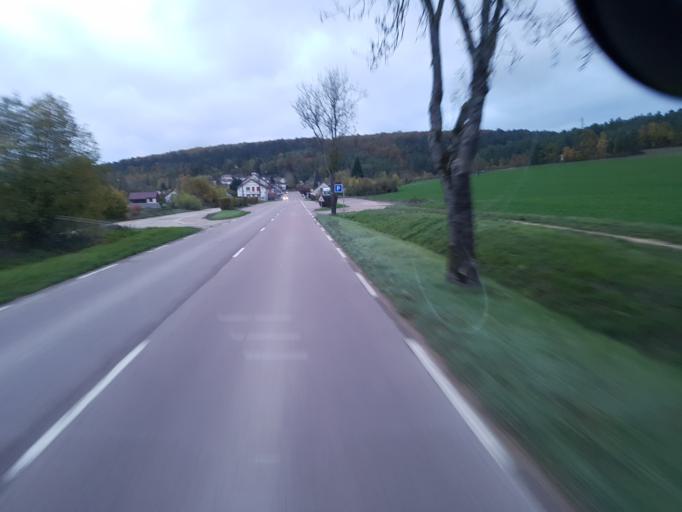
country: FR
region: Champagne-Ardenne
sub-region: Departement de l'Aube
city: Mussy-sur-Seine
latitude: 47.9924
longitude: 4.4836
